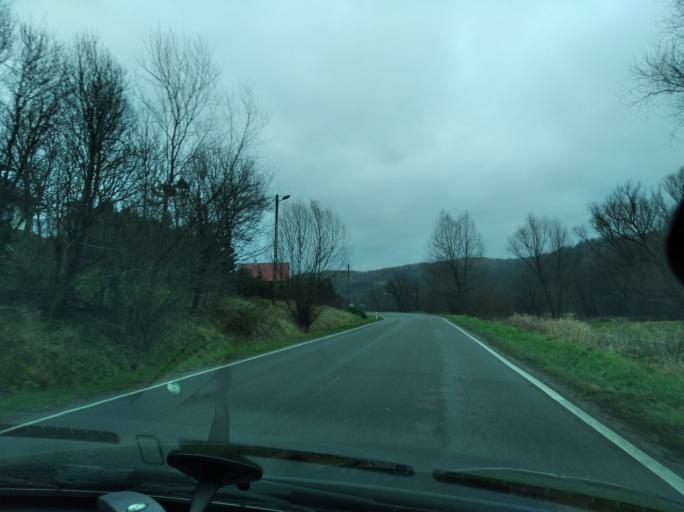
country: PL
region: Subcarpathian Voivodeship
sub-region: Powiat przeworski
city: Manasterz
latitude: 49.9213
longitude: 22.3128
